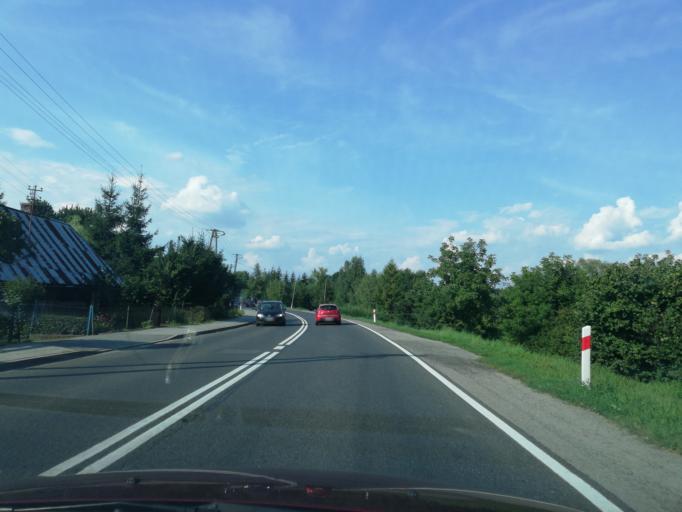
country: PL
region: Lesser Poland Voivodeship
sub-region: Powiat brzeski
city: Czchow
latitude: 49.8141
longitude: 20.6809
